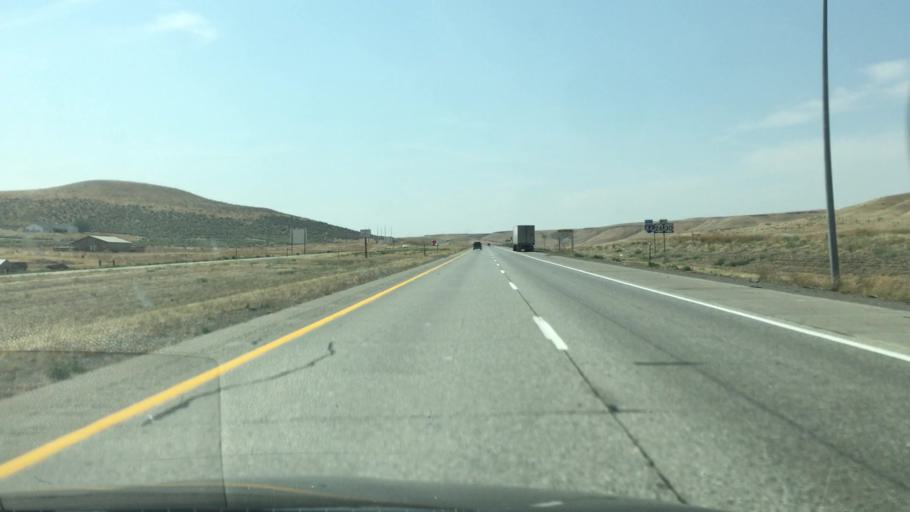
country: US
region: Idaho
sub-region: Elmore County
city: Glenns Ferry
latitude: 42.9627
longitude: -115.3160
